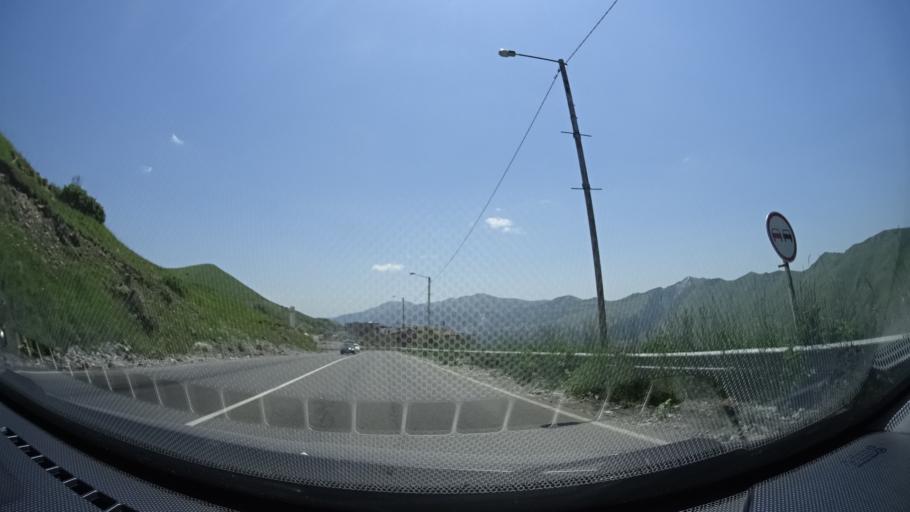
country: GE
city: Gudauri
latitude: 42.4673
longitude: 44.4806
